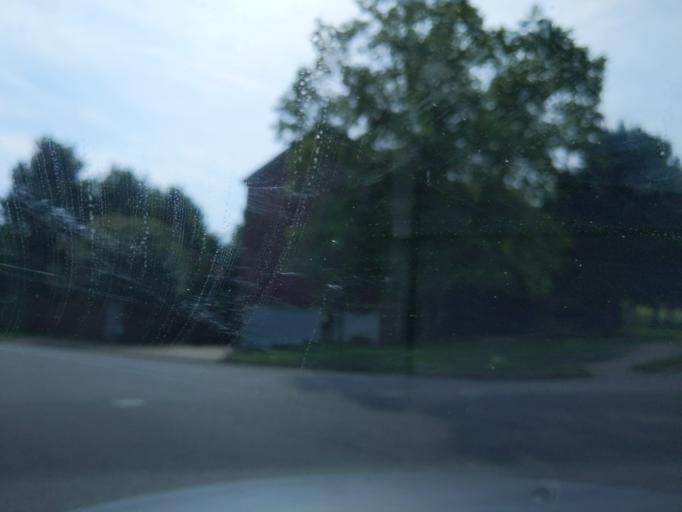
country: US
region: Tennessee
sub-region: Williamson County
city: Brentwood Estates
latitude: 36.0228
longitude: -86.7498
